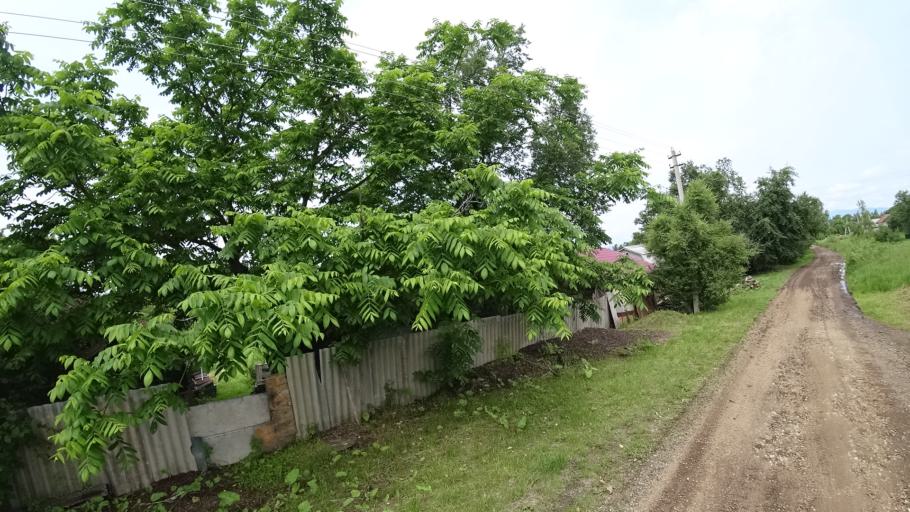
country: RU
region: Primorskiy
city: Novosysoyevka
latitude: 44.2449
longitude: 133.3796
